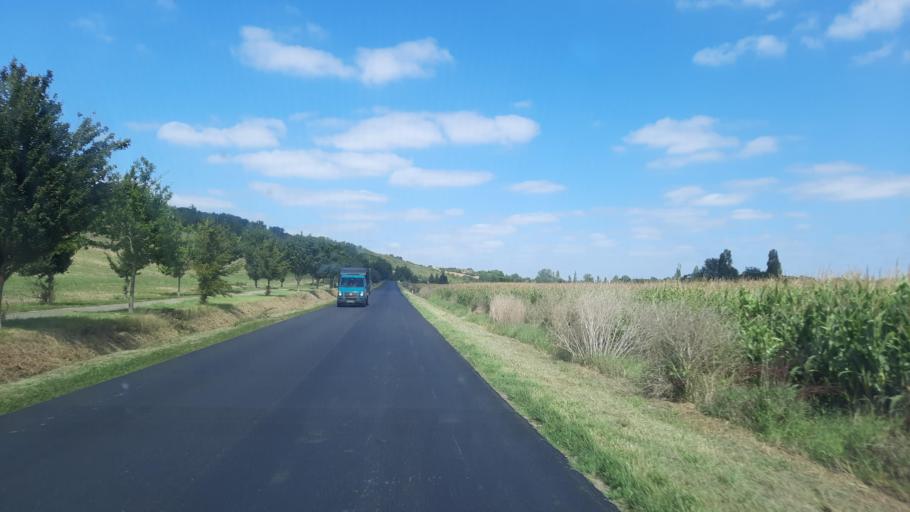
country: FR
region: Midi-Pyrenees
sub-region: Departement du Gers
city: Lombez
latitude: 43.4653
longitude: 0.8913
